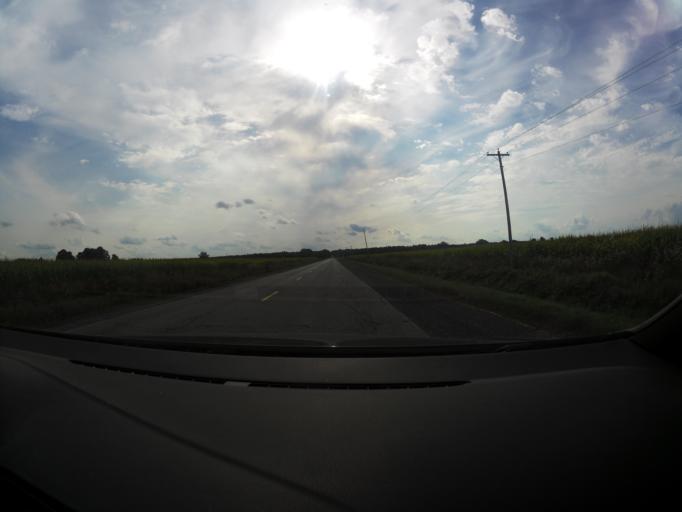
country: CA
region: Ontario
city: Carleton Place
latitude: 45.3528
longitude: -76.1287
